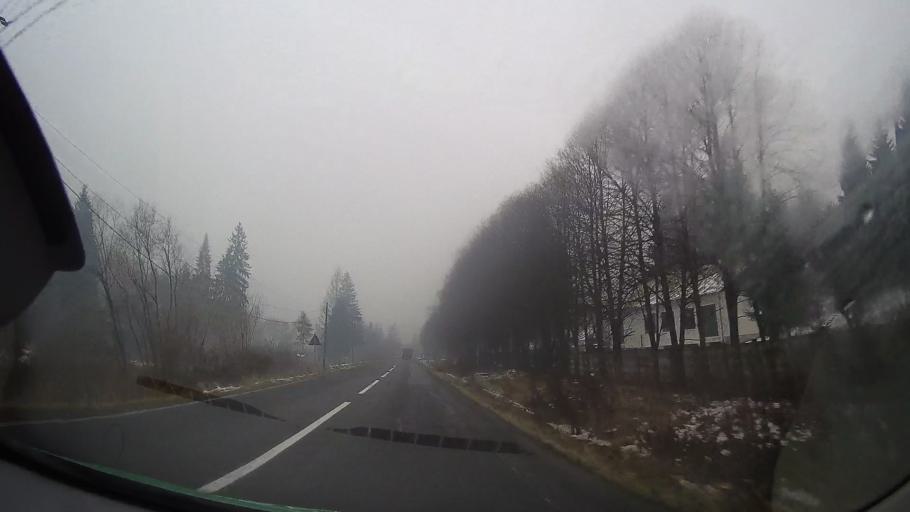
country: RO
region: Harghita
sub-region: Municipiul Gheorgheni
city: Gheorgheni
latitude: 46.7460
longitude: 25.6759
